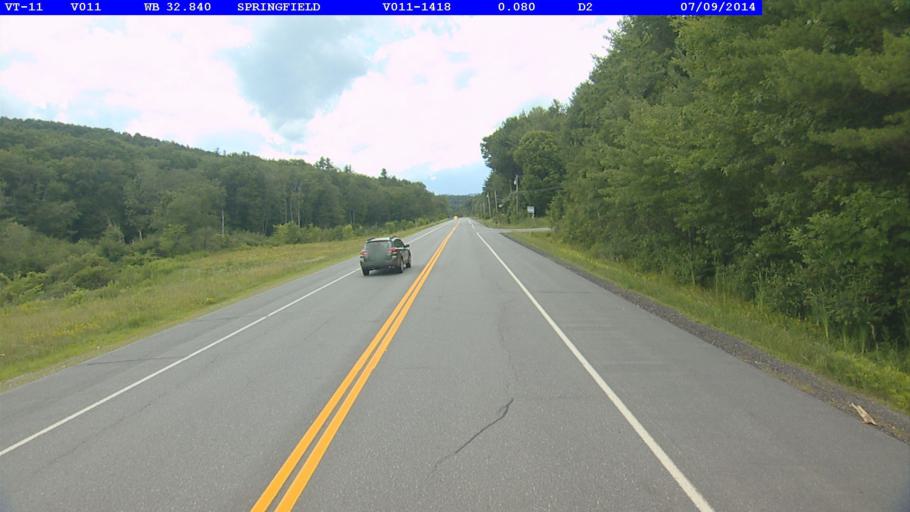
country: US
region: Vermont
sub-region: Windsor County
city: Chester
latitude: 43.2790
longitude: -72.5469
